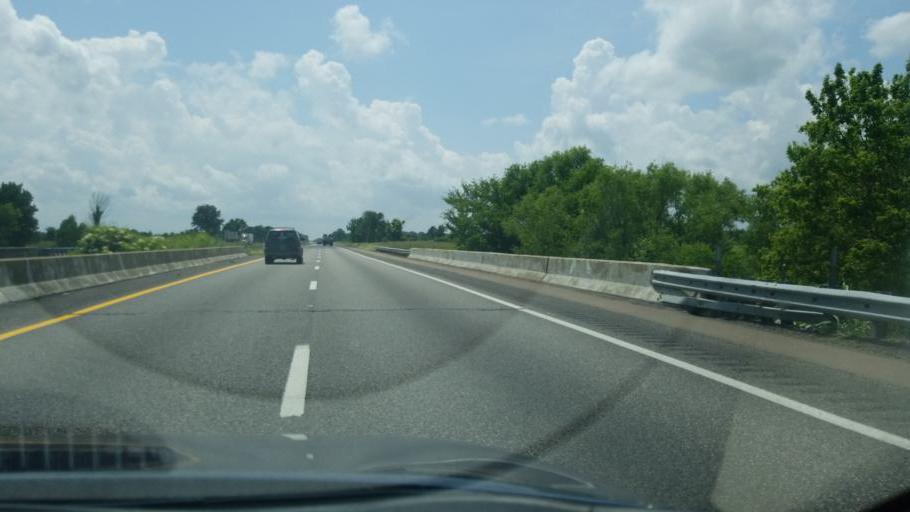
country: US
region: Tennessee
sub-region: Madison County
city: Jackson
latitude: 35.6374
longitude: -88.9349
